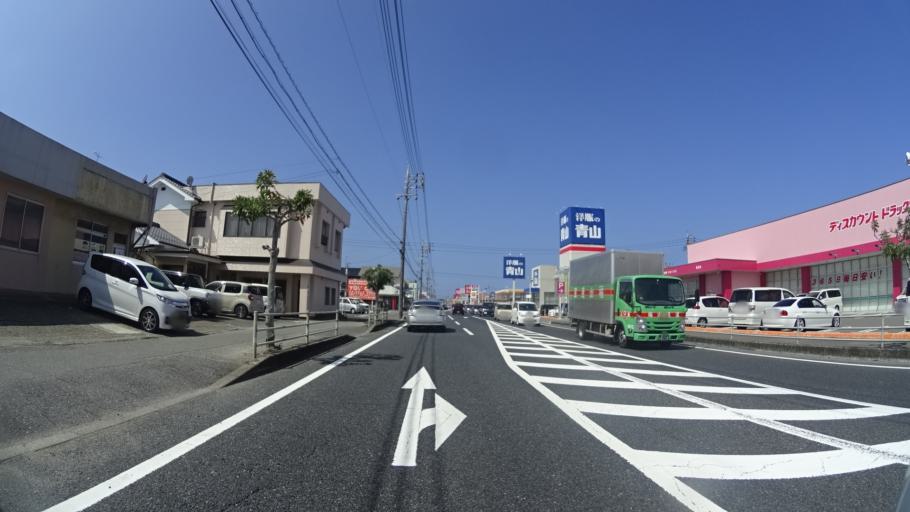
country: JP
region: Shimane
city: Masuda
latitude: 34.6893
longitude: 131.8202
